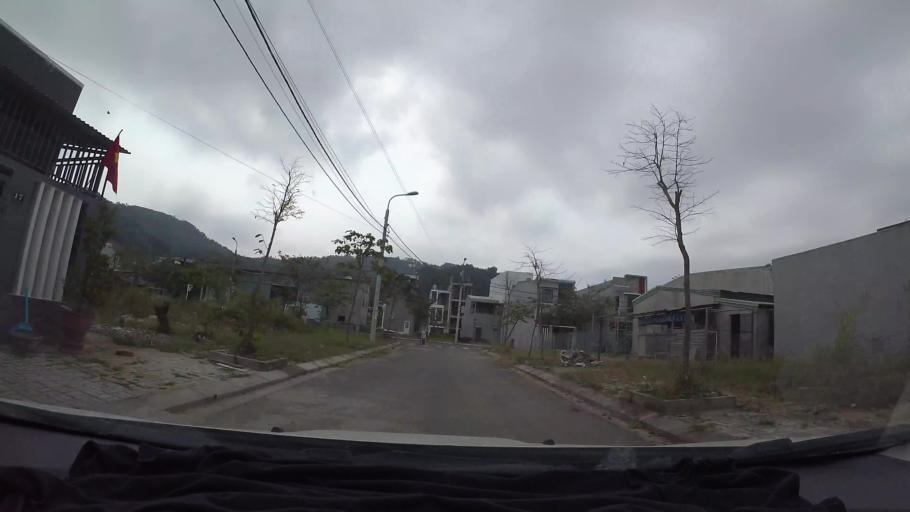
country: VN
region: Da Nang
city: Cam Le
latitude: 16.0377
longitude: 108.1746
